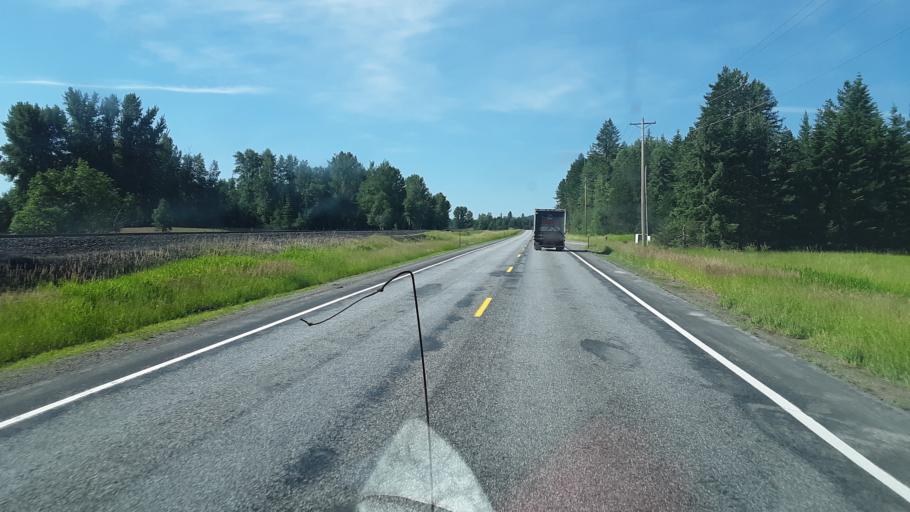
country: US
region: Idaho
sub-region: Bonner County
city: Ponderay
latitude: 48.4593
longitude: -116.4740
